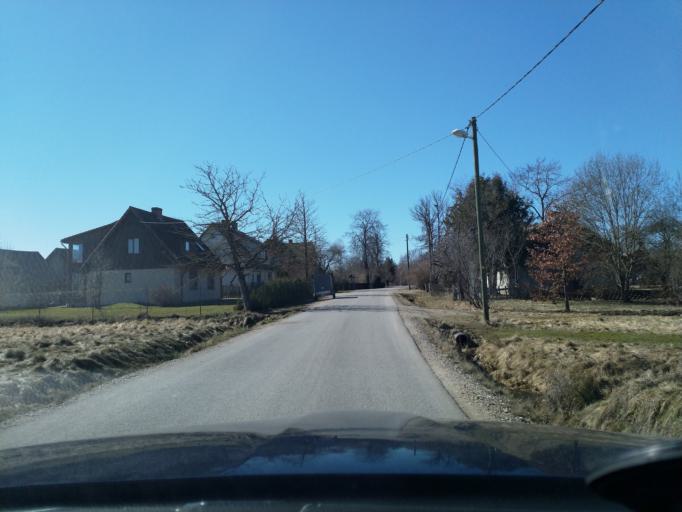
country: LV
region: Kuldigas Rajons
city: Kuldiga
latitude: 56.9636
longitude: 21.9879
